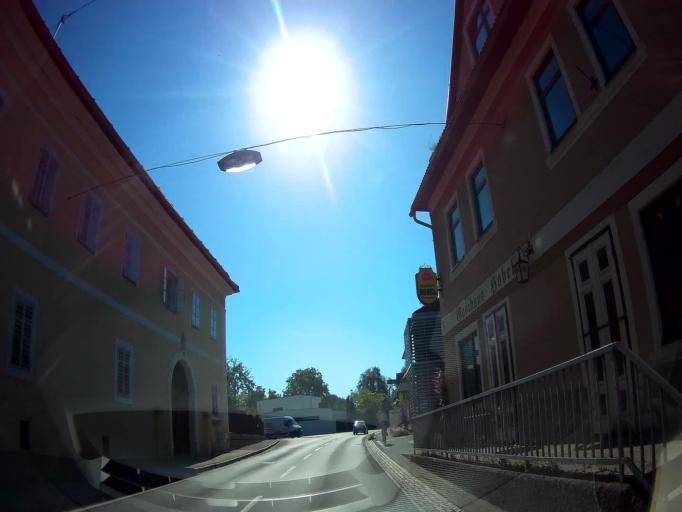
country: AT
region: Carinthia
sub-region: Politischer Bezirk Volkermarkt
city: Eberndorf
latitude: 46.5905
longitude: 14.6412
